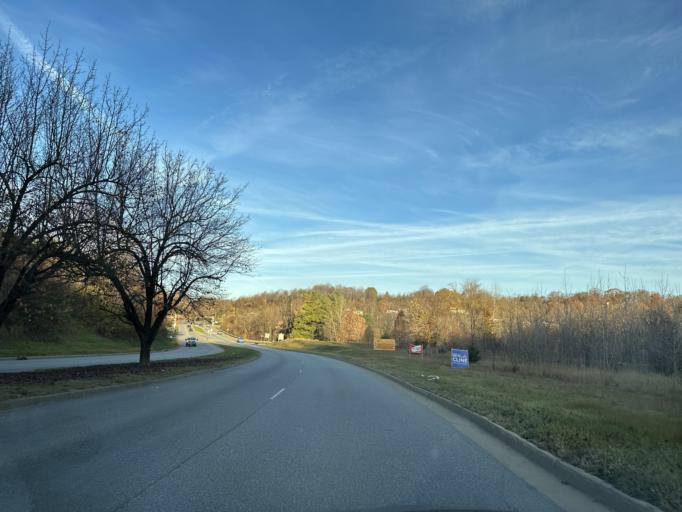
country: US
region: Virginia
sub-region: City of Staunton
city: Staunton
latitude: 38.1520
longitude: -79.0531
